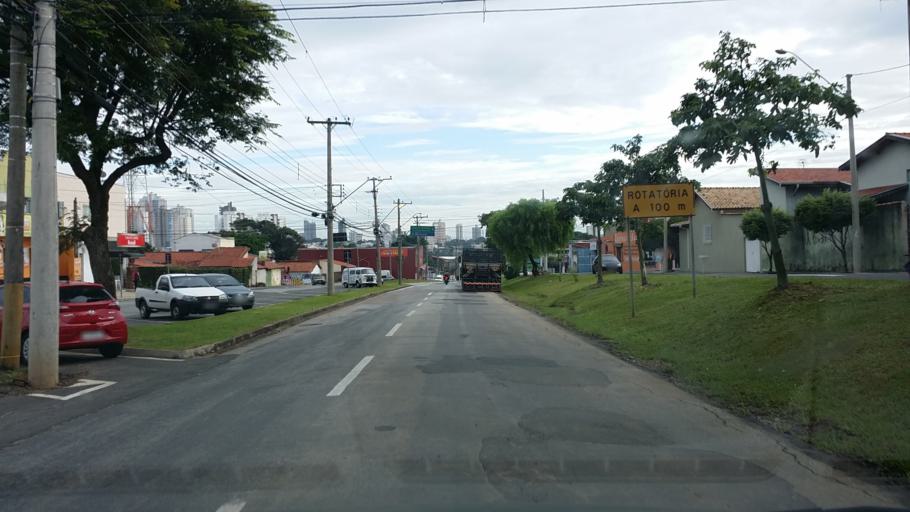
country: BR
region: Sao Paulo
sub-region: Indaiatuba
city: Indaiatuba
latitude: -23.1012
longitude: -47.2202
